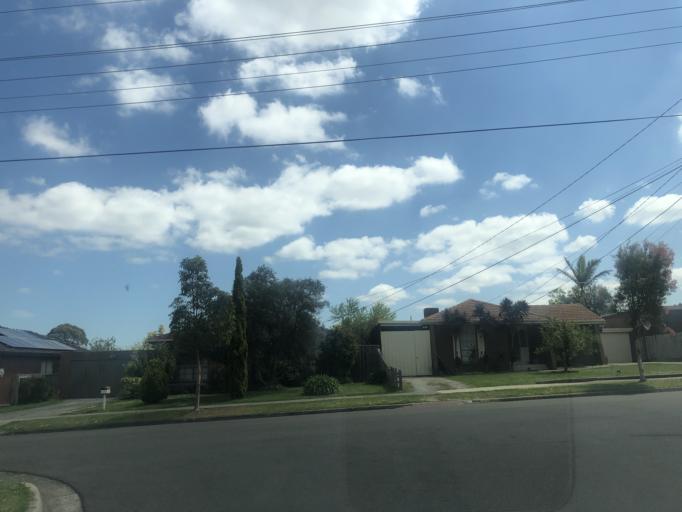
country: AU
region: Victoria
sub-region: Monash
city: Mulgrave
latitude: -37.9087
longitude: 145.1839
